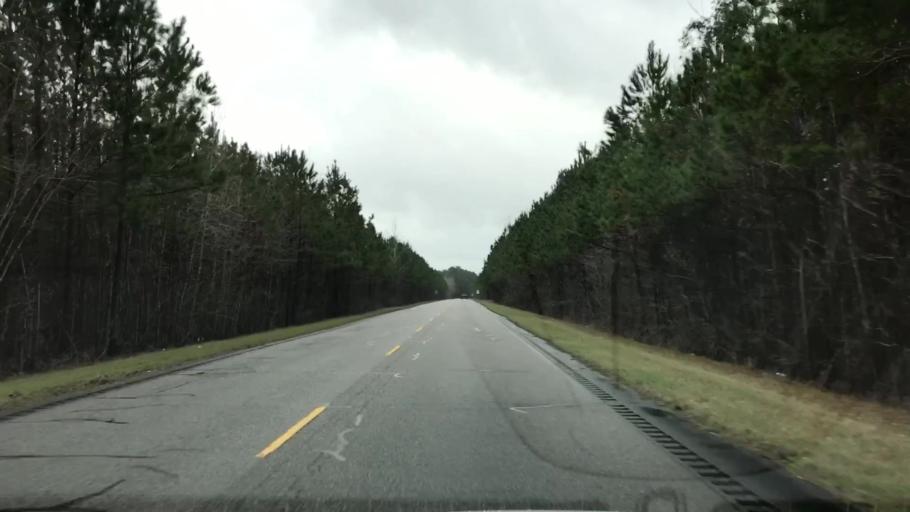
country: US
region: South Carolina
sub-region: Williamsburg County
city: Andrews
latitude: 33.5673
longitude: -79.4525
